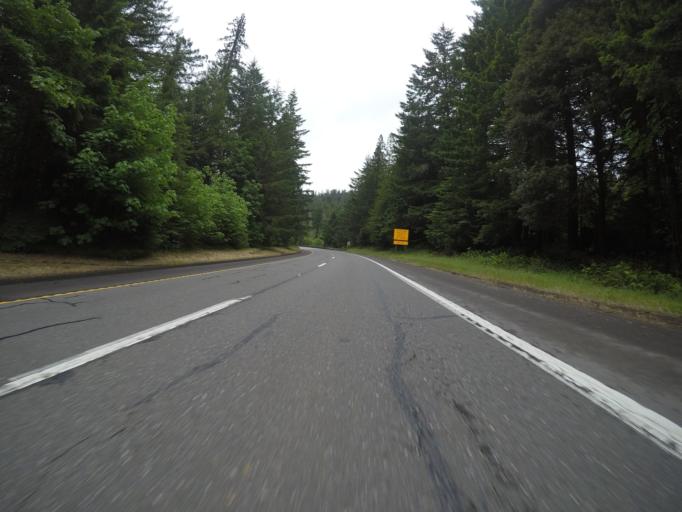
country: US
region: California
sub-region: Humboldt County
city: Rio Dell
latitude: 40.4417
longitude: -124.0388
